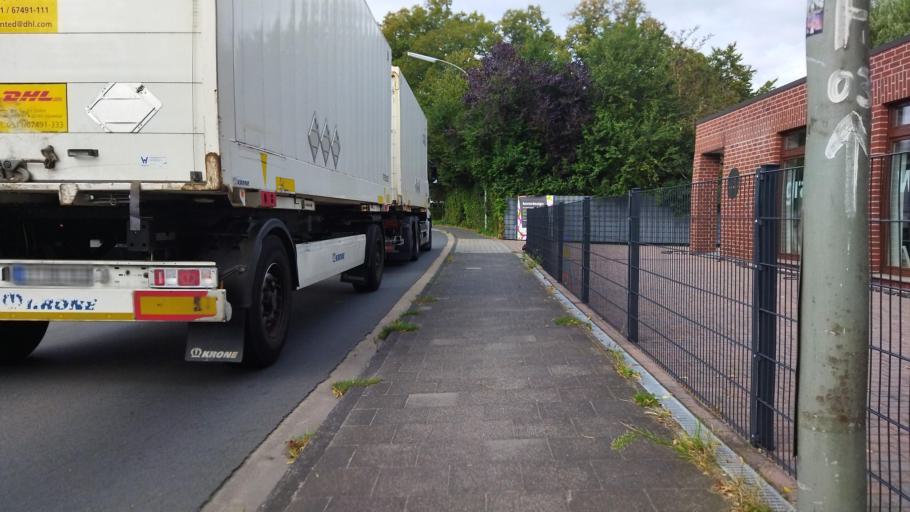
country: DE
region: North Rhine-Westphalia
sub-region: Regierungsbezirk Munster
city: Telgte
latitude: 52.0206
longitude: 7.7811
